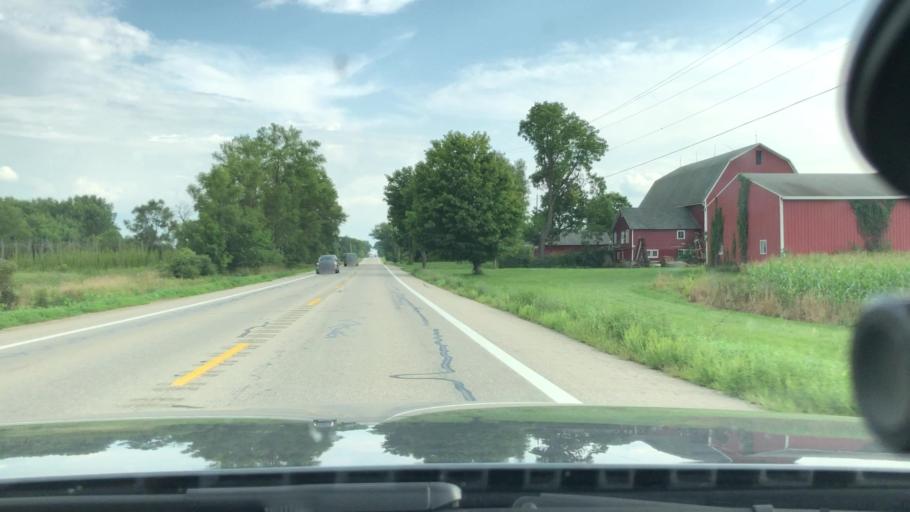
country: US
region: Michigan
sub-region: Washtenaw County
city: Manchester
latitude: 42.2056
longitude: -84.0329
